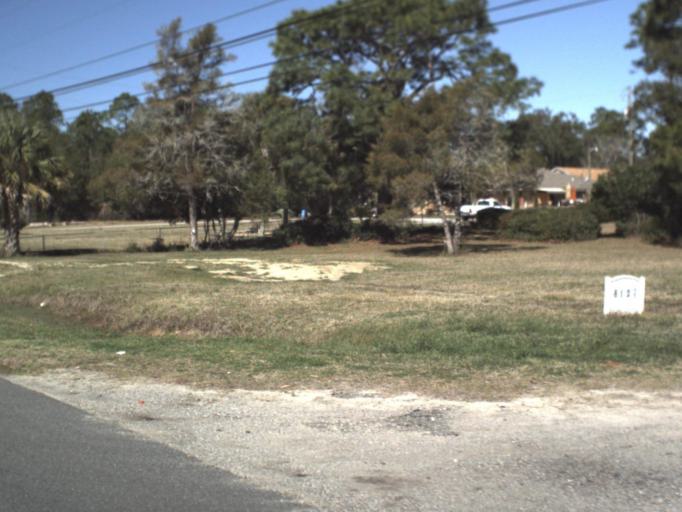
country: US
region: Florida
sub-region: Bay County
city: Callaway
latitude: 30.1529
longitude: -85.5520
